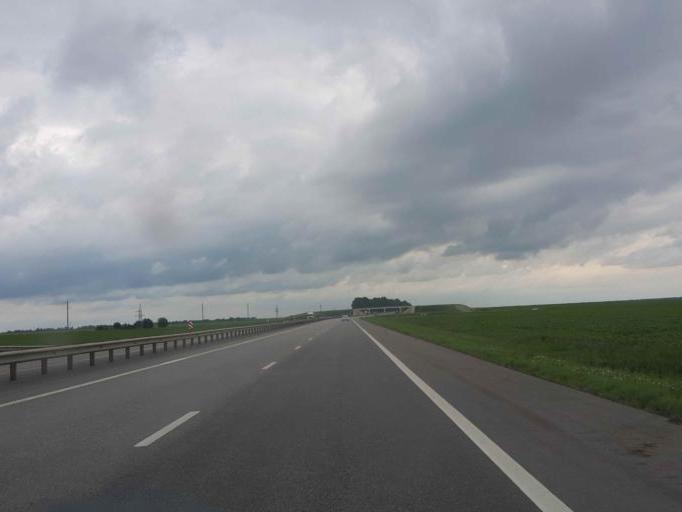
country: RU
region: Tambov
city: Selezni
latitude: 52.8268
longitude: 40.9051
